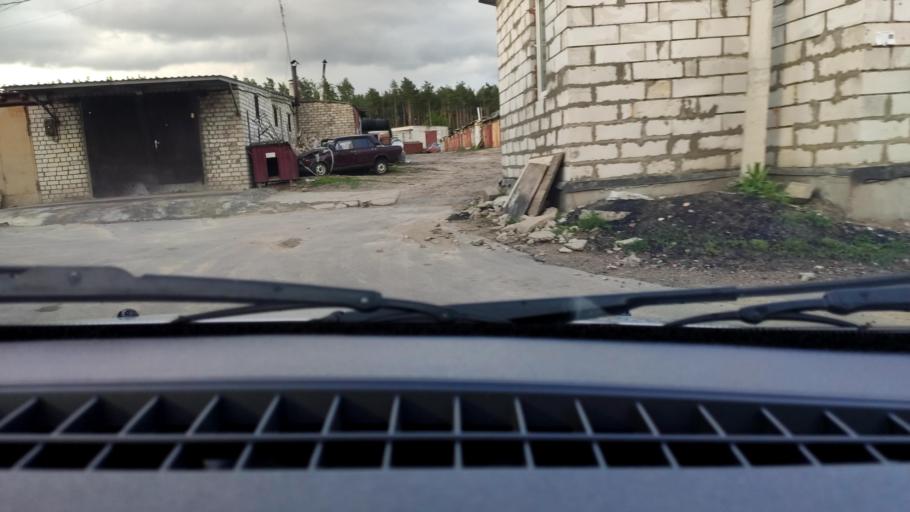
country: RU
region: Voronezj
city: Pridonskoy
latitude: 51.6404
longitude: 39.1138
